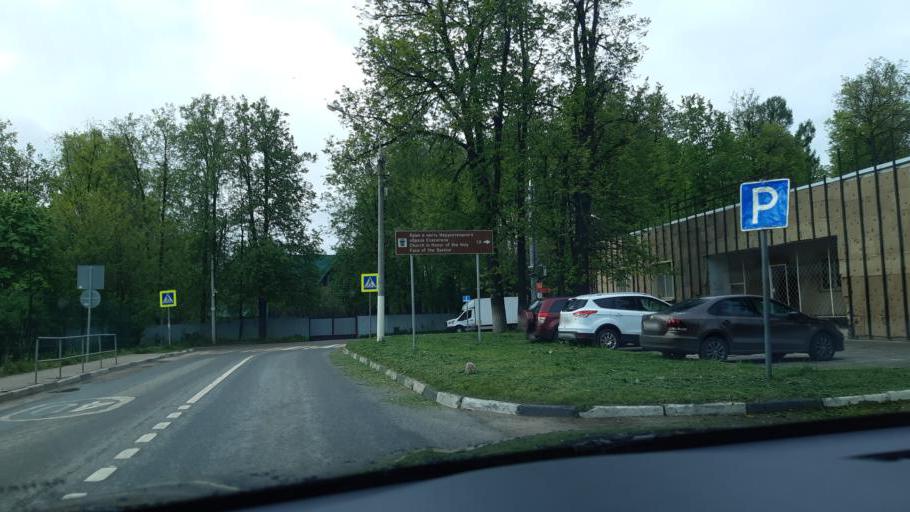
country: RU
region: Moskovskaya
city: Dolgoprudnyy
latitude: 55.9528
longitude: 37.4913
